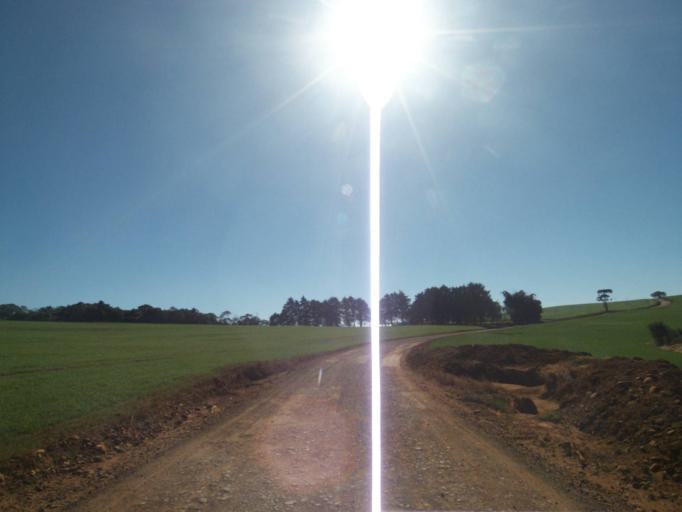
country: BR
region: Parana
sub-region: Tibagi
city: Tibagi
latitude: -24.6099
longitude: -50.6059
